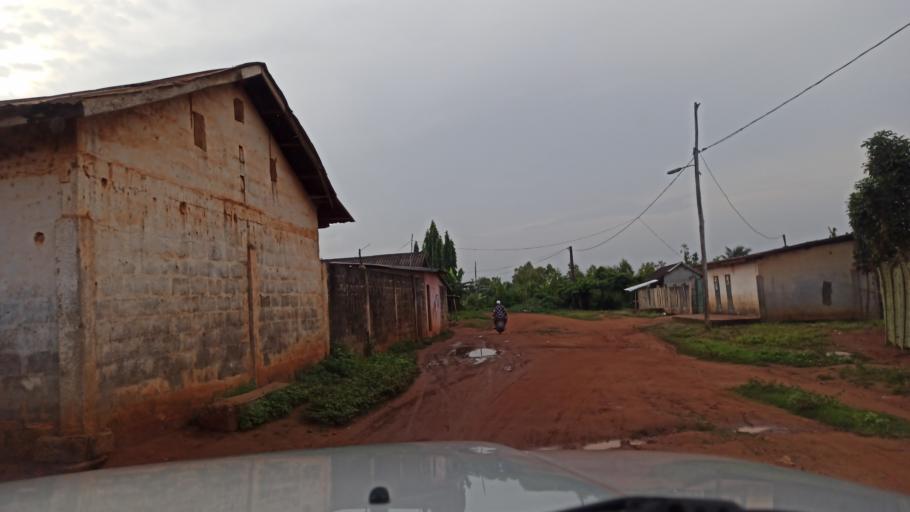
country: BJ
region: Queme
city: Porto-Novo
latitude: 6.5027
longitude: 2.6985
